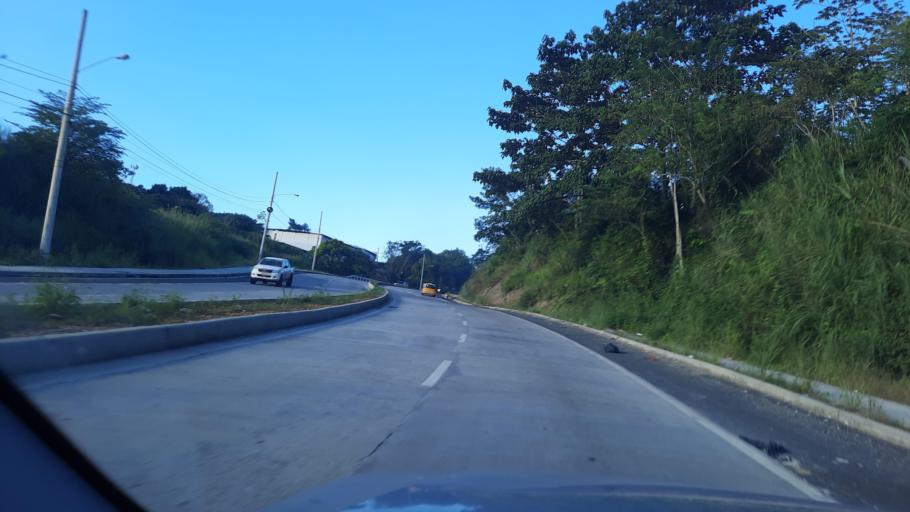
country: PA
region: Panama
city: Las Cumbres
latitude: 9.1040
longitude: -79.5309
